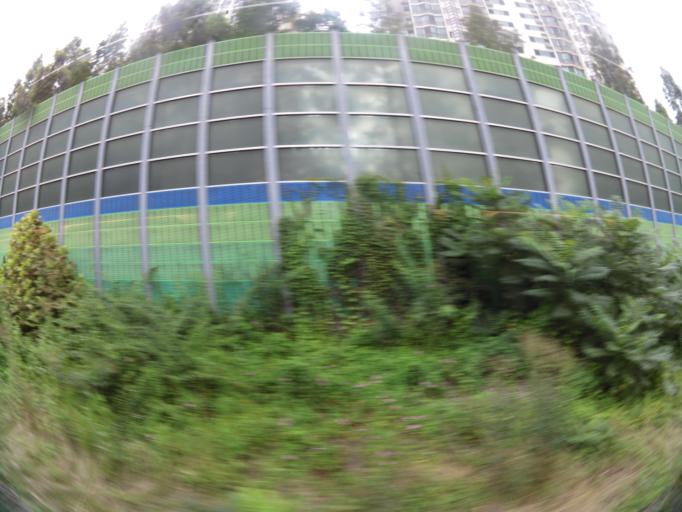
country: KR
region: Seoul
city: Seoul
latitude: 37.5138
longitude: 126.9298
